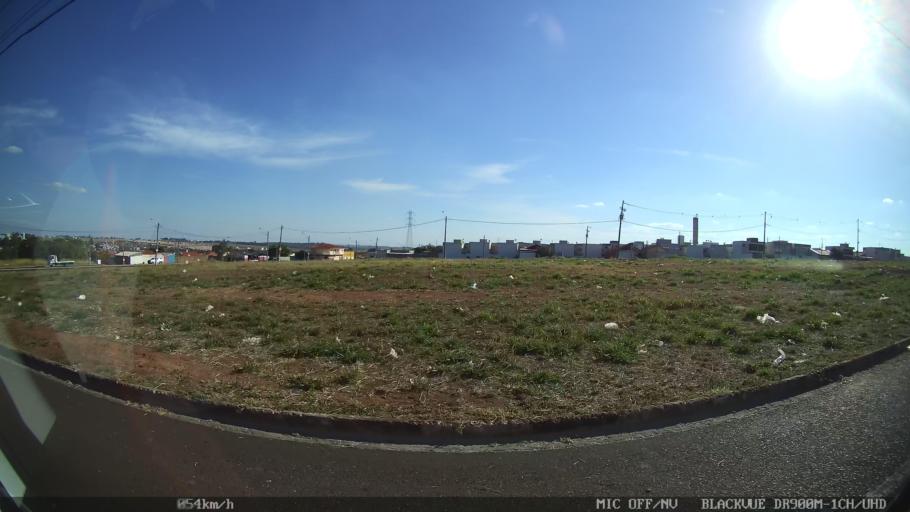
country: BR
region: Sao Paulo
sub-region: Franca
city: Franca
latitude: -20.5138
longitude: -47.4402
